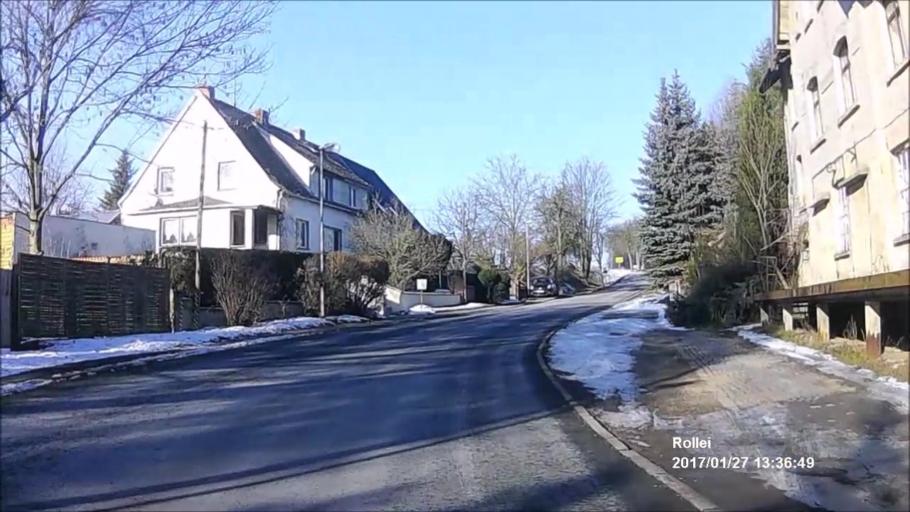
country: DE
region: Thuringia
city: Neunheilingen
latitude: 51.1953
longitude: 10.6749
